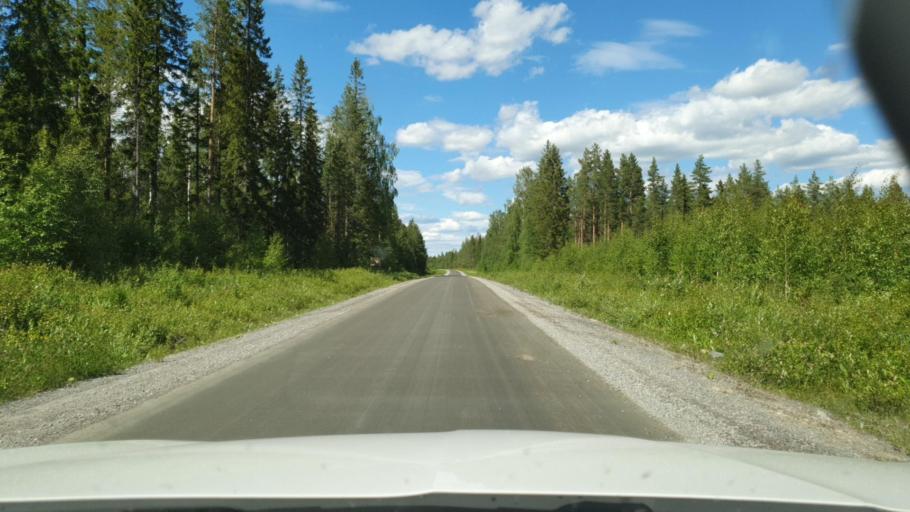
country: SE
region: Vaesterbotten
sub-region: Skelleftea Kommun
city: Forsbacka
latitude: 64.8006
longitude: 20.5038
